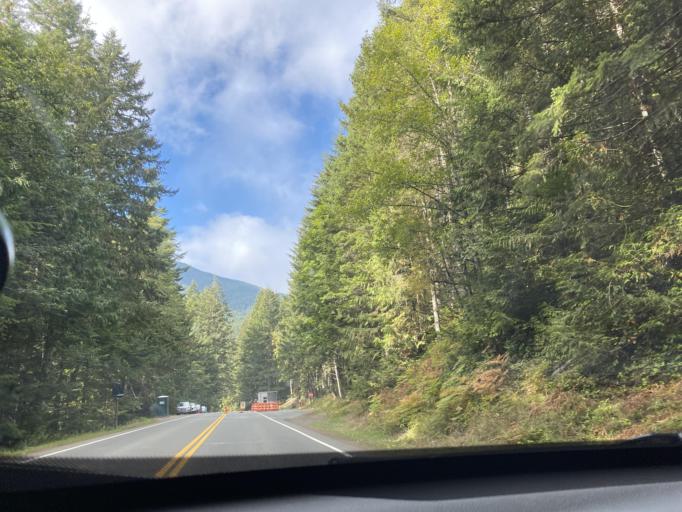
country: US
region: Washington
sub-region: Clallam County
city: Port Angeles
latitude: 48.0416
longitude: -123.4244
